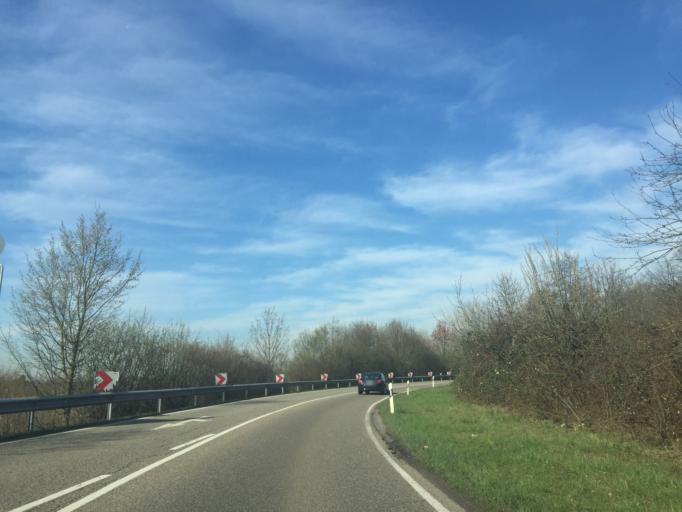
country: DE
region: Baden-Wuerttemberg
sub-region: Karlsruhe Region
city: Dossenheim
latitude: 49.4397
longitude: 8.6646
